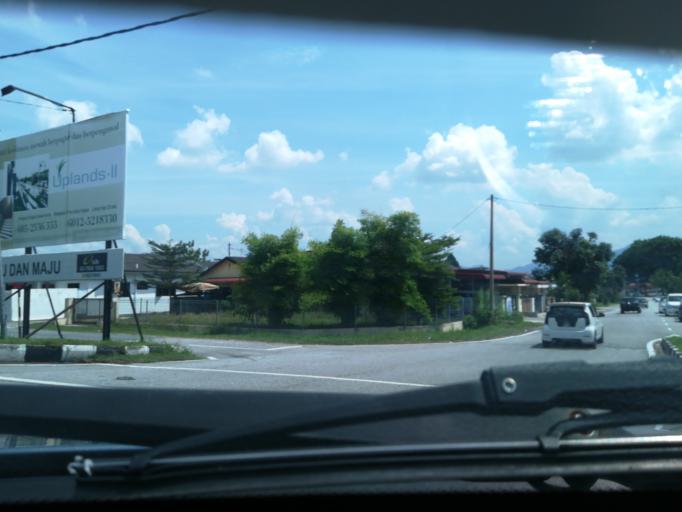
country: MY
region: Perak
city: Ipoh
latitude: 4.6124
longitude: 101.1174
